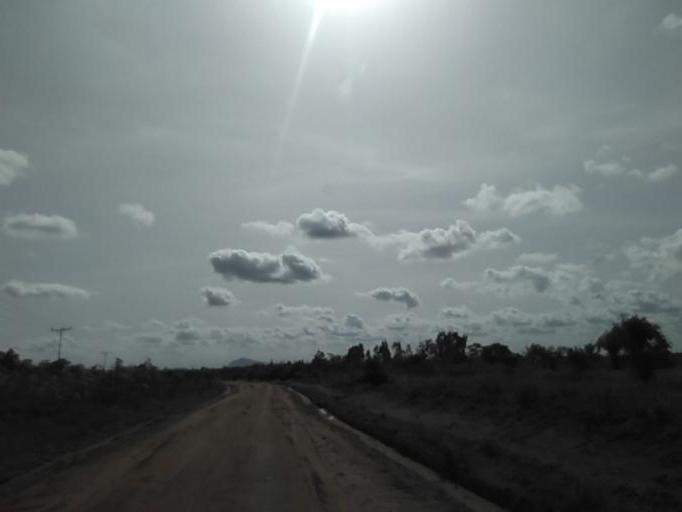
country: GH
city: Akropong
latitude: 6.0298
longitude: 0.3633
